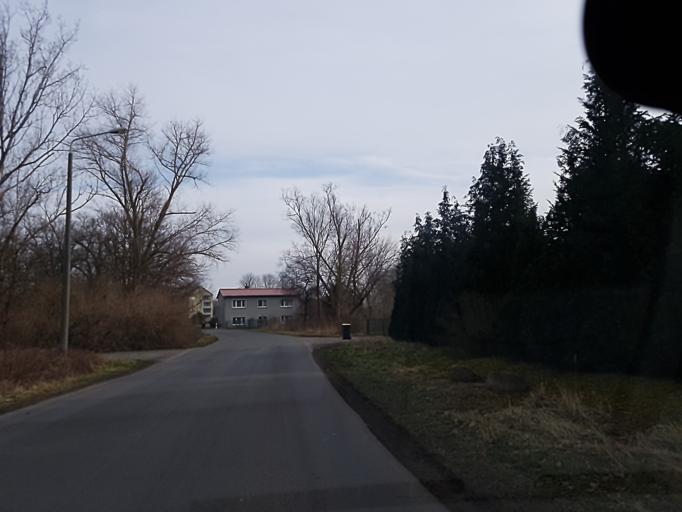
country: DE
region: Brandenburg
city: Doberlug-Kirchhain
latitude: 51.6230
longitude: 13.5574
